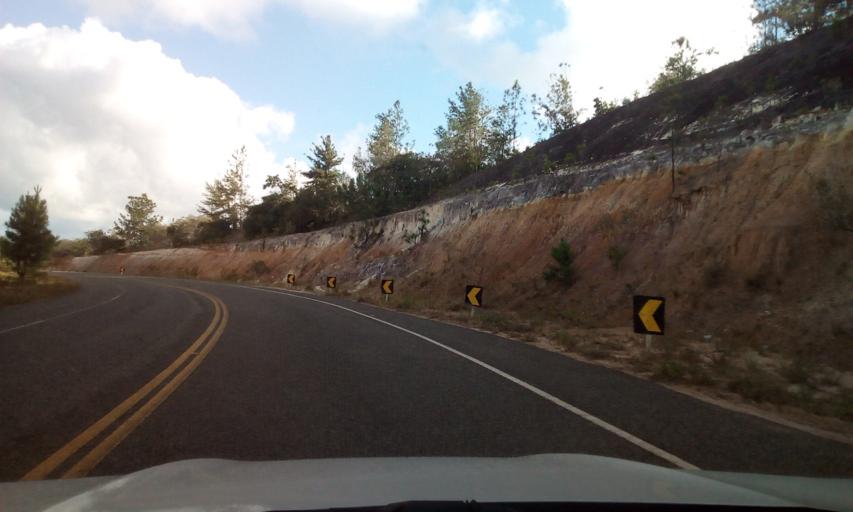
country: BR
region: Bahia
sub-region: Conde
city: Conde
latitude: -12.0958
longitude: -37.7730
